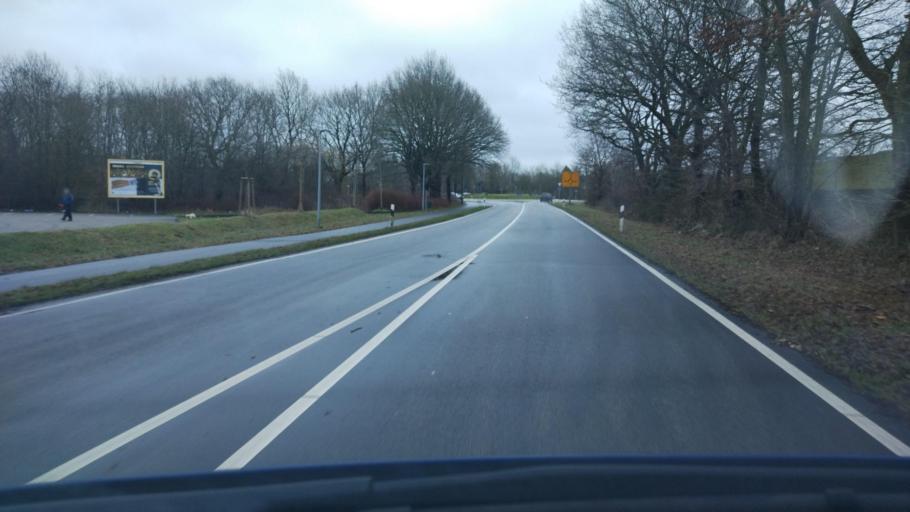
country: DE
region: Schleswig-Holstein
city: Kropp
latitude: 54.4165
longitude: 9.4967
